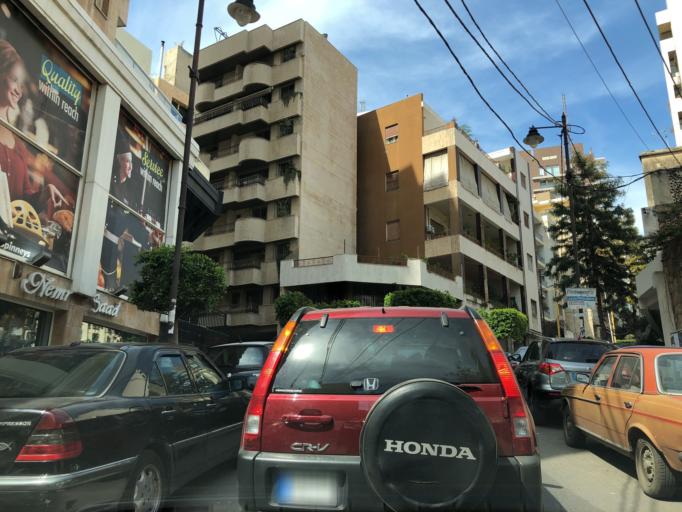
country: LB
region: Beyrouth
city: Beirut
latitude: 33.8846
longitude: 35.5189
